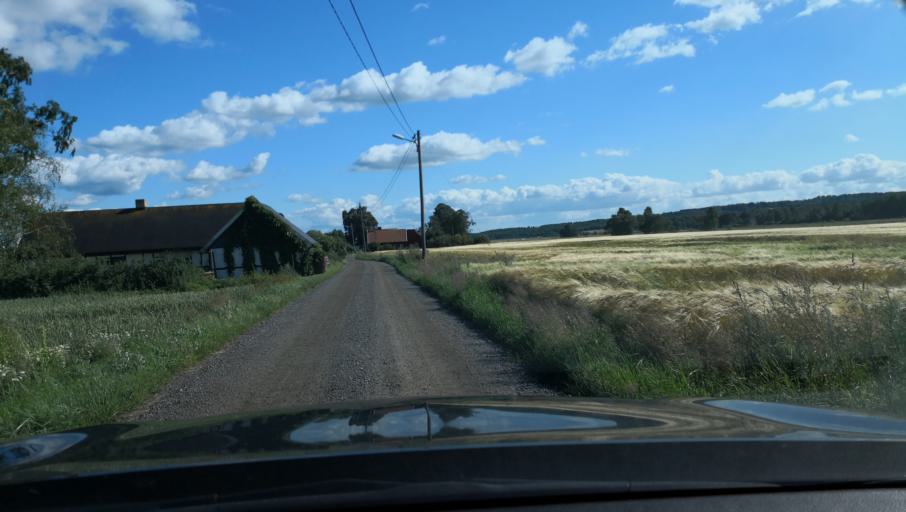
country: SE
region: Skane
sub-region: Kristianstads Kommun
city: Degeberga
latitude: 55.8100
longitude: 14.1891
